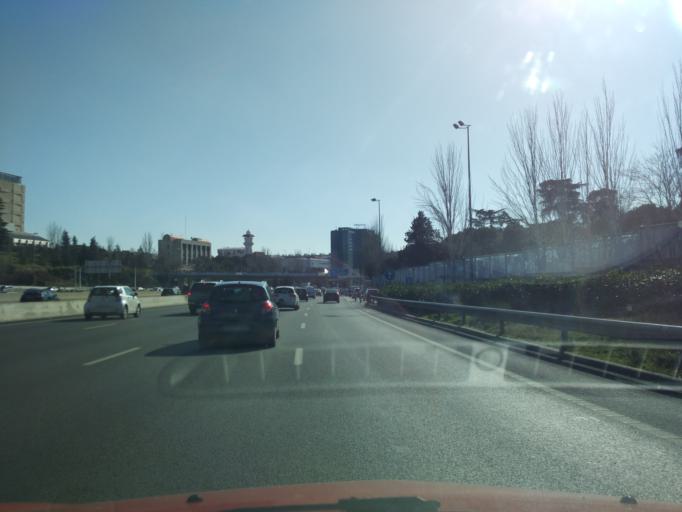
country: ES
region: Madrid
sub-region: Provincia de Madrid
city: Ciudad Lineal
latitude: 40.4433
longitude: -3.6602
